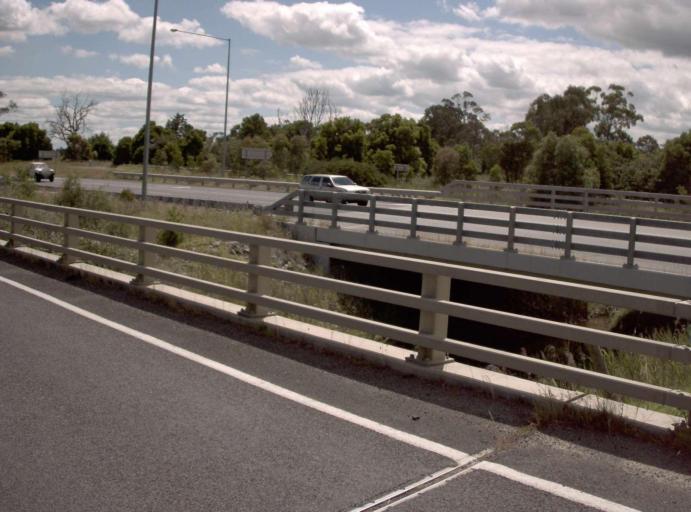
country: AU
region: Victoria
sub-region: Cardinia
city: Koo-Wee-Rup
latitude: -38.3706
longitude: 145.5635
